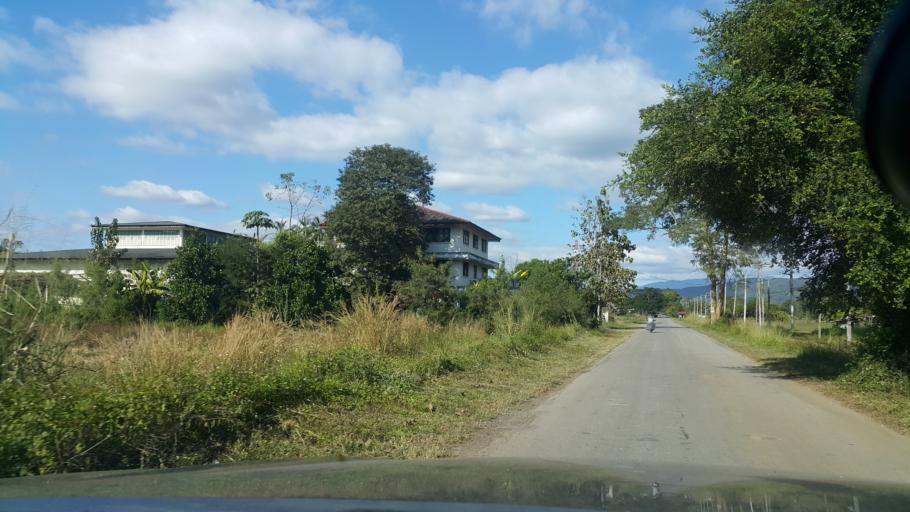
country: TH
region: Chiang Mai
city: Mae On
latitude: 18.7747
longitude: 99.2537
